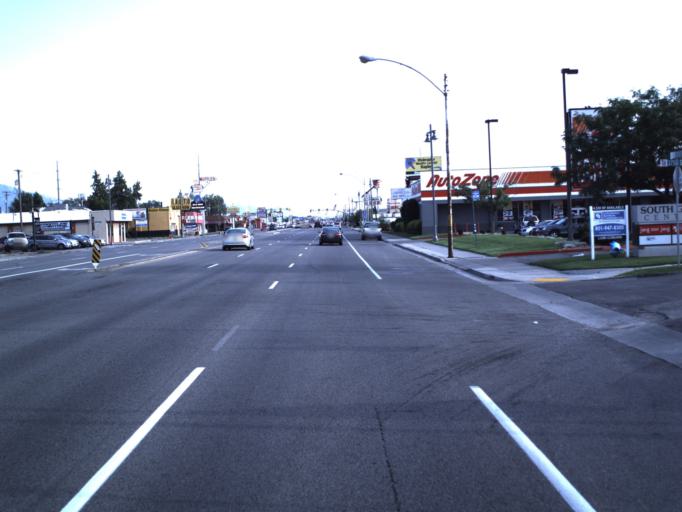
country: US
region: Utah
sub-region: Salt Lake County
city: Centerfield
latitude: 40.6899
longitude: -111.8884
